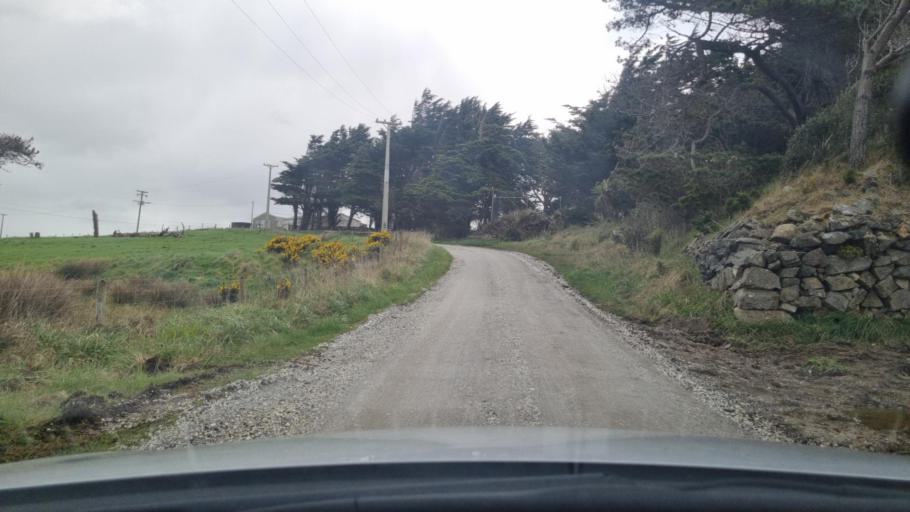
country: NZ
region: Southland
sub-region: Invercargill City
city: Bluff
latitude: -46.5462
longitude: 168.2987
